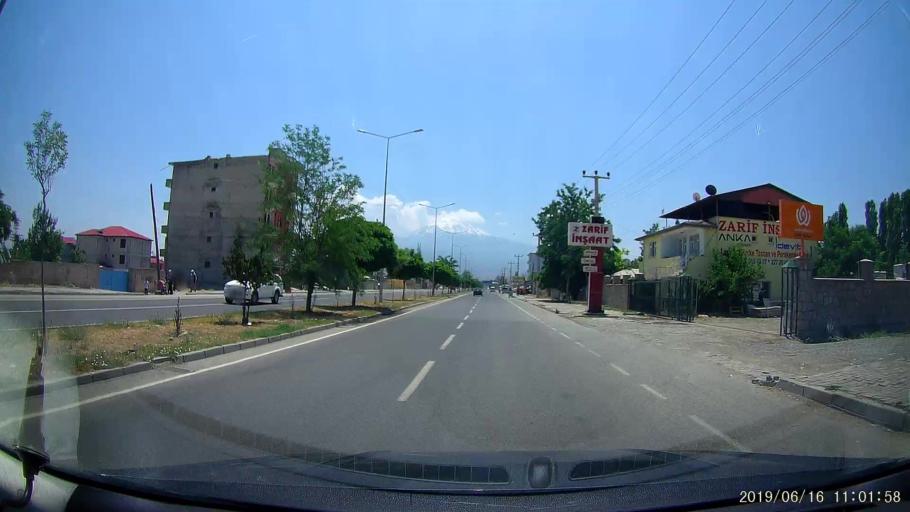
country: TR
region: Igdir
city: Igdir
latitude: 39.9110
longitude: 44.0552
